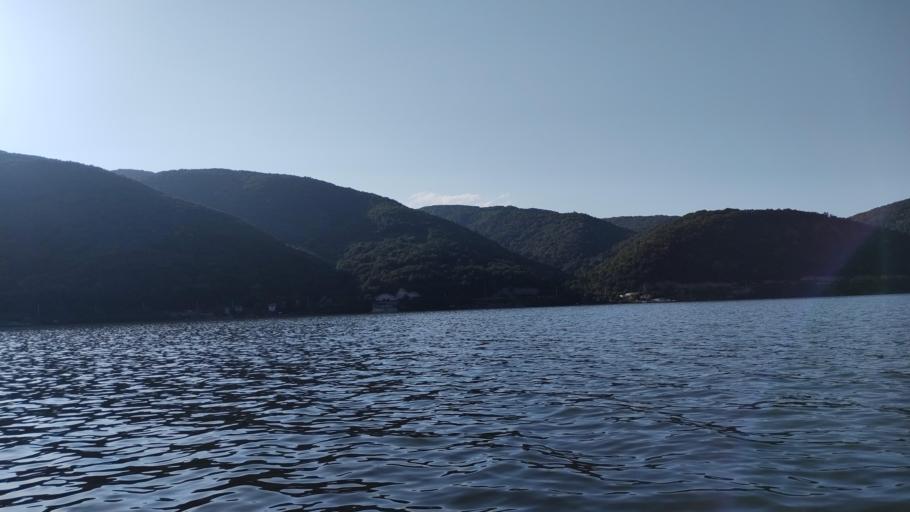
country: RO
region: Mehedinti
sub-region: Comuna Dubova
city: Dubova
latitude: 44.5744
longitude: 22.2437
